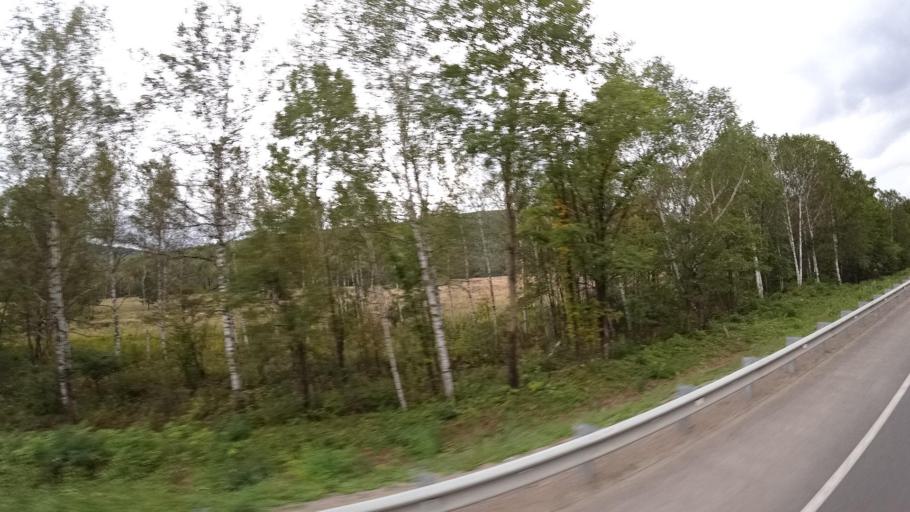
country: RU
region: Jewish Autonomous Oblast
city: Khingansk
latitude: 48.9843
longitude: 131.1446
